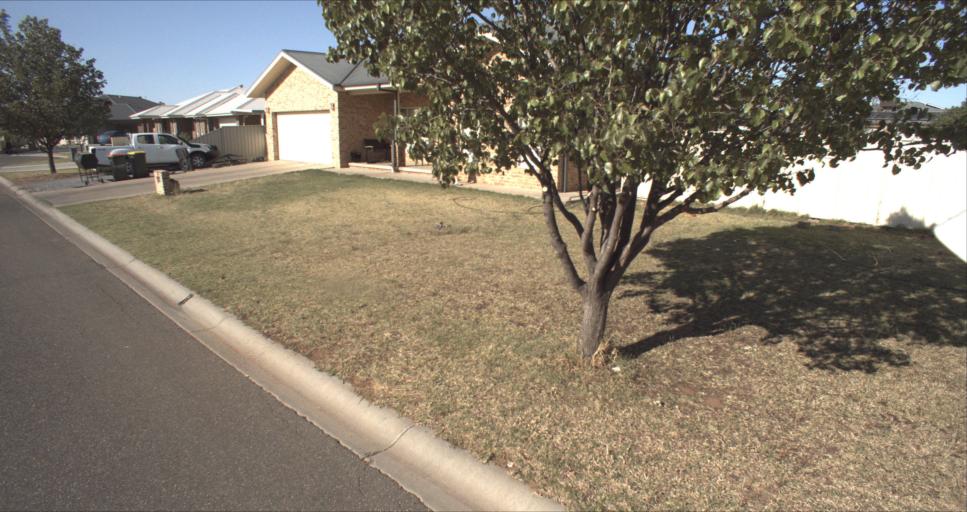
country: AU
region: New South Wales
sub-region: Leeton
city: Leeton
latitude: -34.5366
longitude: 146.4044
